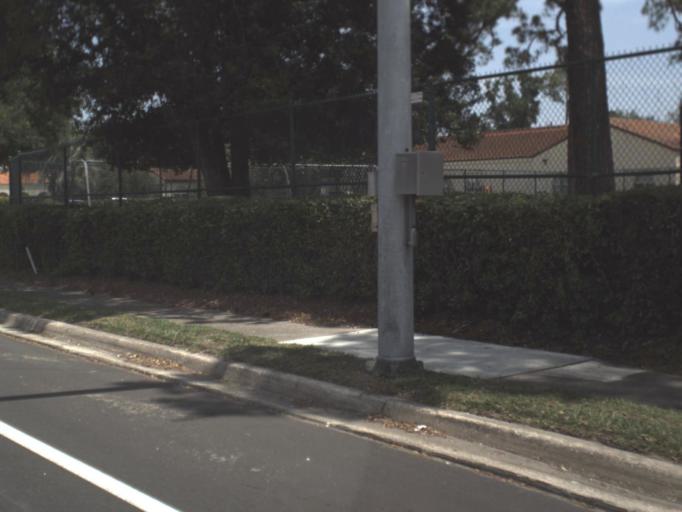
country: US
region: Florida
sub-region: Duval County
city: Jacksonville
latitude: 30.2430
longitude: -81.6262
